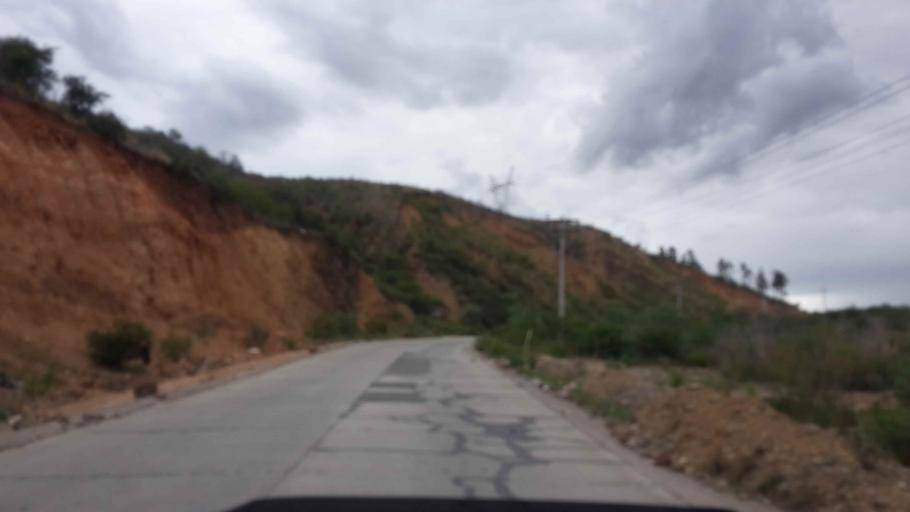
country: BO
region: Cochabamba
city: Cochabamba
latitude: -17.5311
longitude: -66.1975
